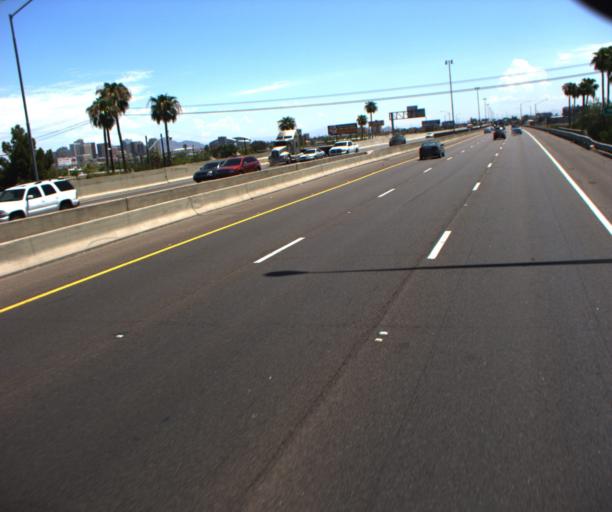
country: US
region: Arizona
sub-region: Maricopa County
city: Phoenix
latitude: 33.4287
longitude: -112.1007
